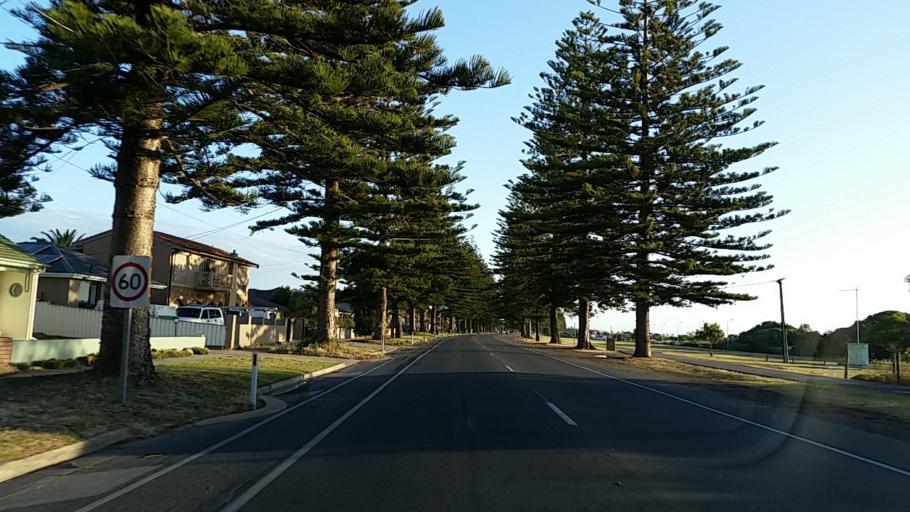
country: AU
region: South Australia
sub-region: Port Adelaide Enfield
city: Birkenhead
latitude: -34.7972
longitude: 138.4918
